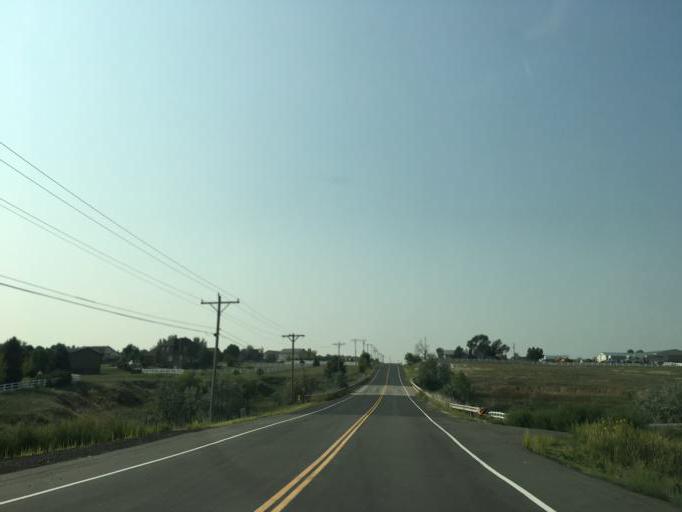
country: US
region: Colorado
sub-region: Adams County
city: Todd Creek
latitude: 39.9799
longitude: -104.8655
